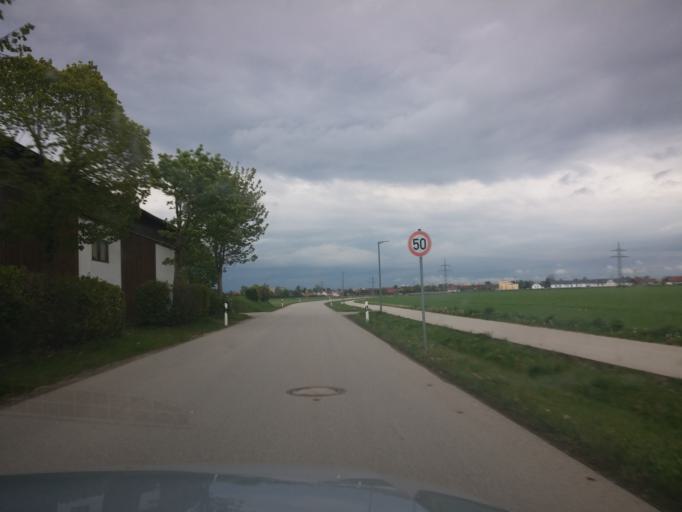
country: DE
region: Bavaria
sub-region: Upper Bavaria
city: Putzbrunn
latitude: 48.0866
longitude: 11.7116
